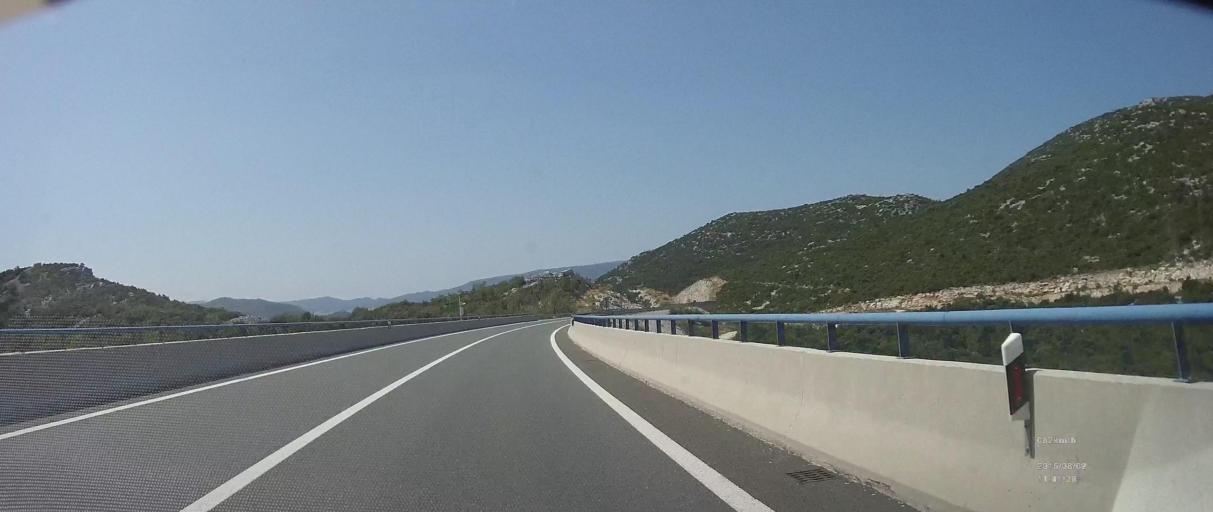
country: HR
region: Dubrovacko-Neretvanska
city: Komin
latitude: 43.0615
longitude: 17.4953
